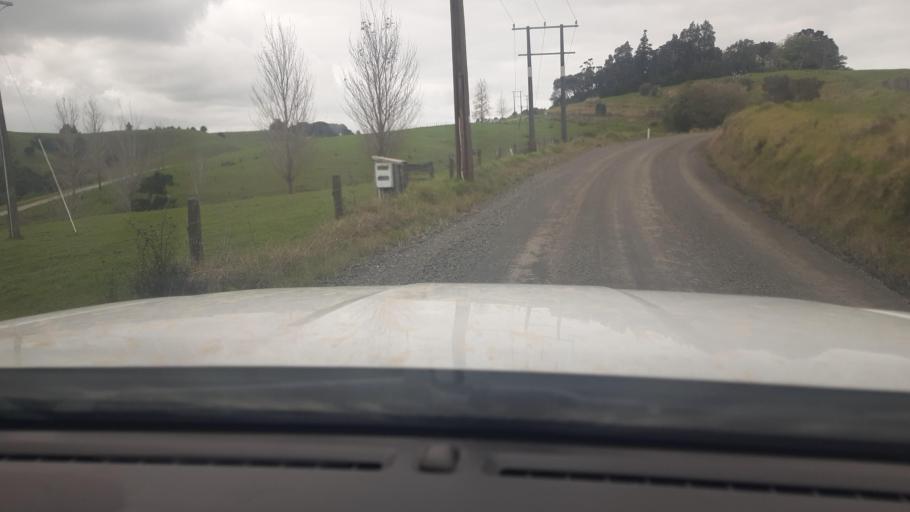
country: NZ
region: Northland
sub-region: Far North District
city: Kaitaia
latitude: -35.0895
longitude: 173.3183
